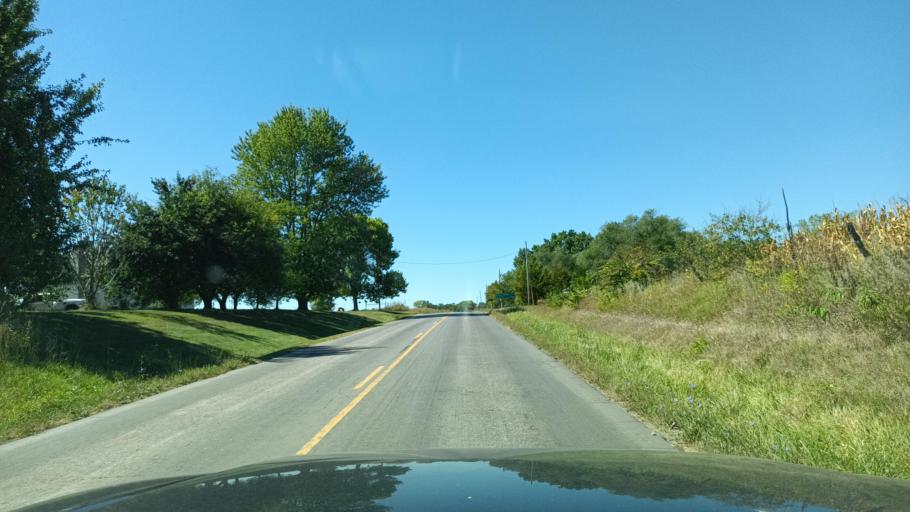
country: US
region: Missouri
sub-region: Macon County
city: La Plata
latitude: 40.0234
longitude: -92.5975
